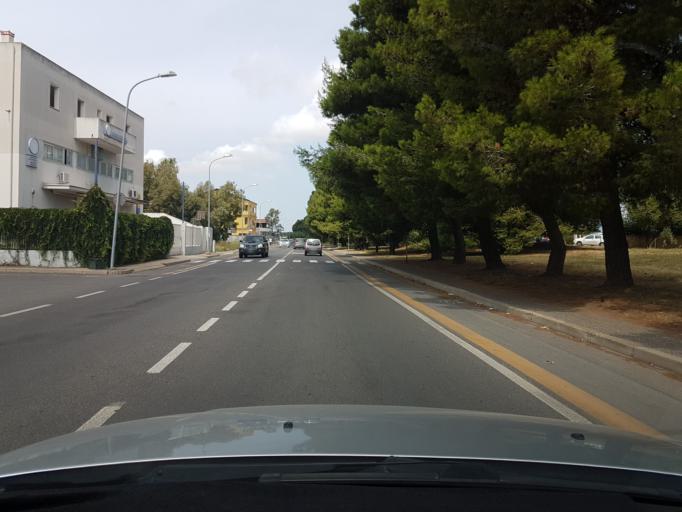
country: IT
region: Sardinia
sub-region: Provincia di Oristano
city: Oristano
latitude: 39.9131
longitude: 8.5898
